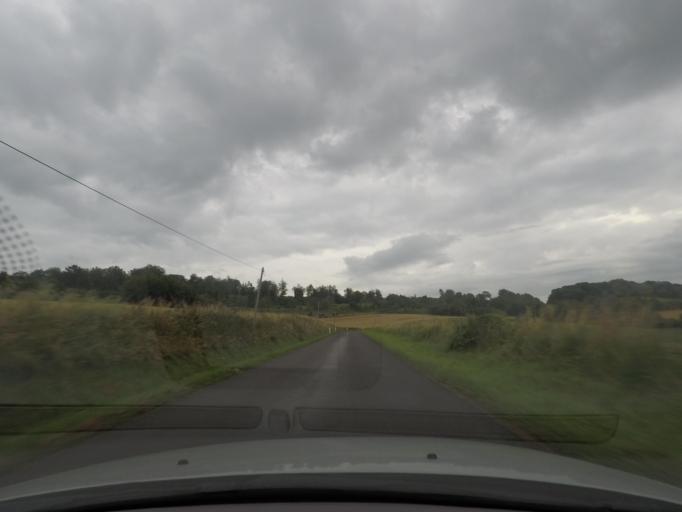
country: FR
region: Haute-Normandie
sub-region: Departement de la Seine-Maritime
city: Neufchatel-en-Bray
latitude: 49.7308
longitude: 1.4652
